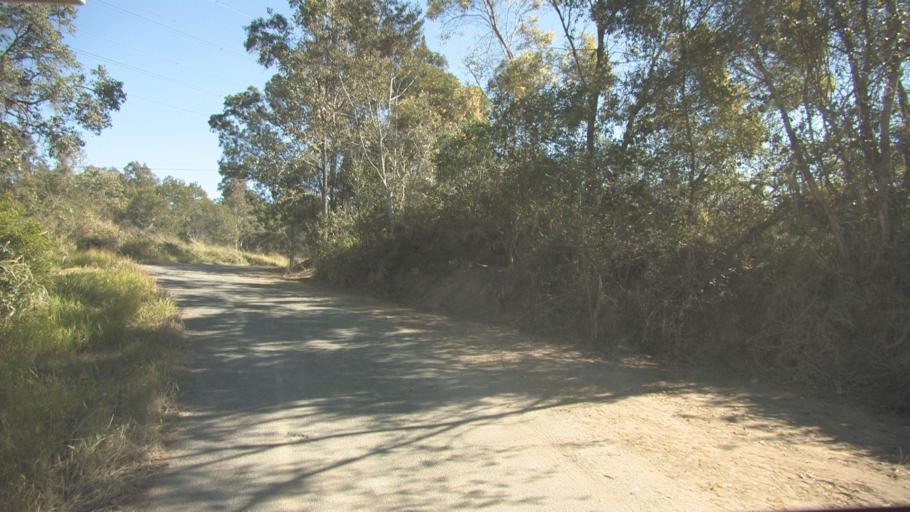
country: AU
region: Queensland
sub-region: Ipswich
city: Springfield Lakes
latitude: -27.7281
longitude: 152.9488
